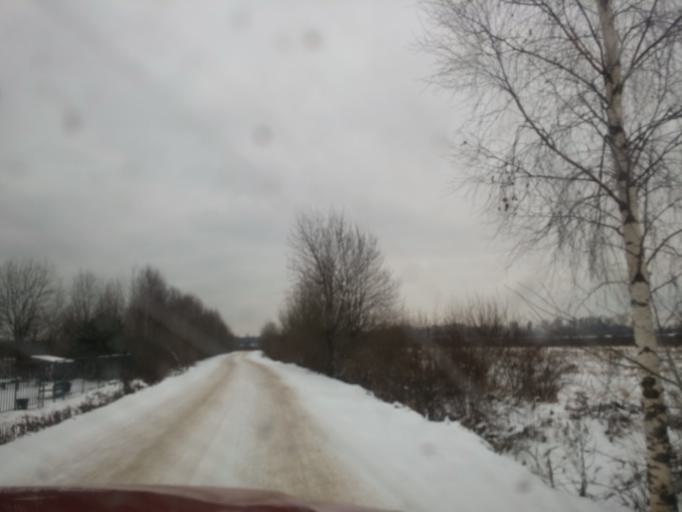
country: RU
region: Moskovskaya
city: Reshetnikovo
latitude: 56.4553
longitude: 36.5504
